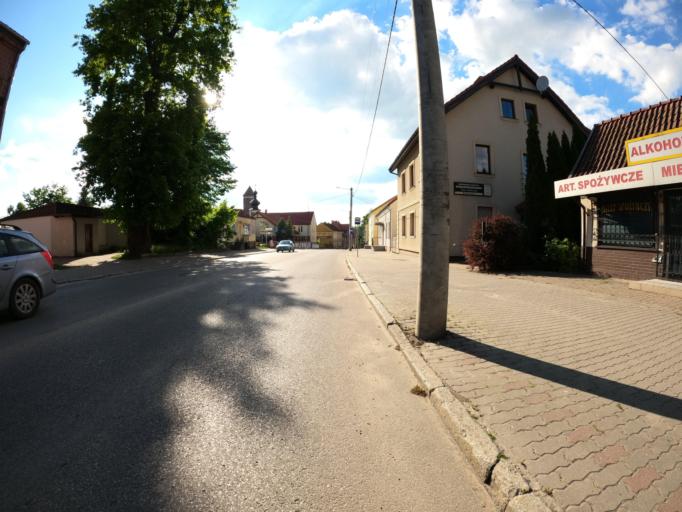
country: PL
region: Warmian-Masurian Voivodeship
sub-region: Powiat lidzbarski
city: Lidzbark Warminski
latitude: 54.1257
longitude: 20.5867
